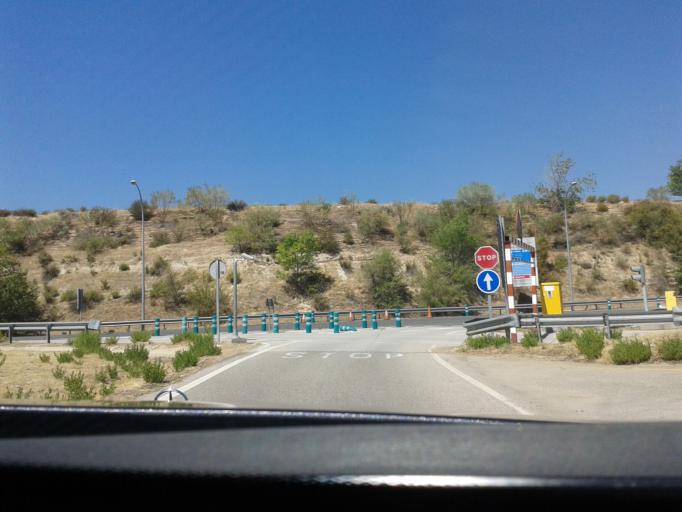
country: ES
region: Madrid
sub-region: Provincia de Madrid
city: Barajas de Madrid
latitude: 40.4875
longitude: -3.5951
